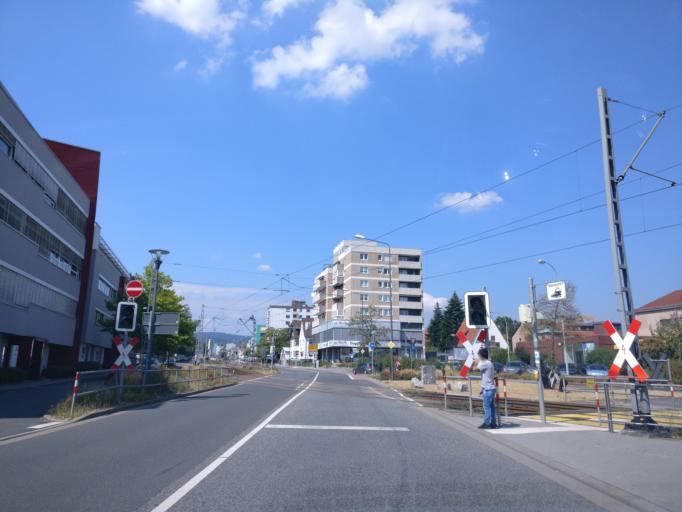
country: DE
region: Hesse
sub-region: Regierungsbezirk Darmstadt
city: Oberursel
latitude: 50.2061
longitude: 8.5780
